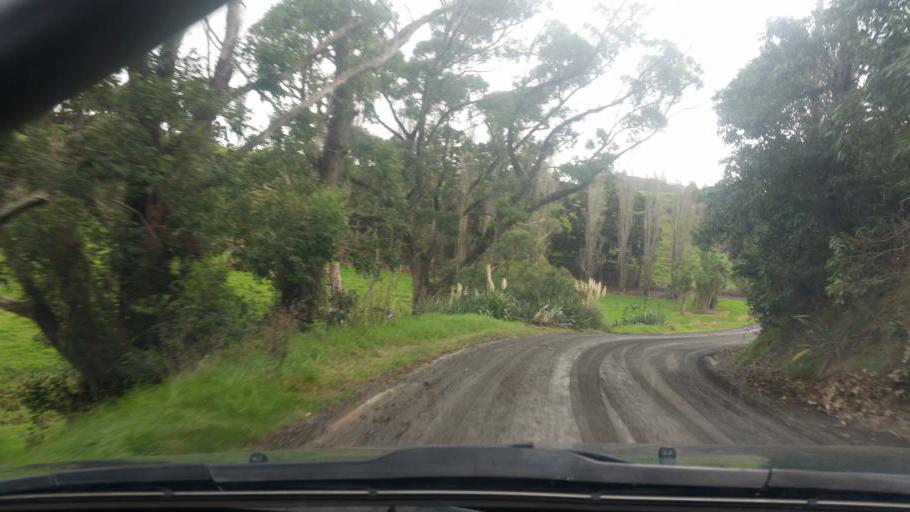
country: NZ
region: Northland
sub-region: Kaipara District
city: Dargaville
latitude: -35.8381
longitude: 173.6609
